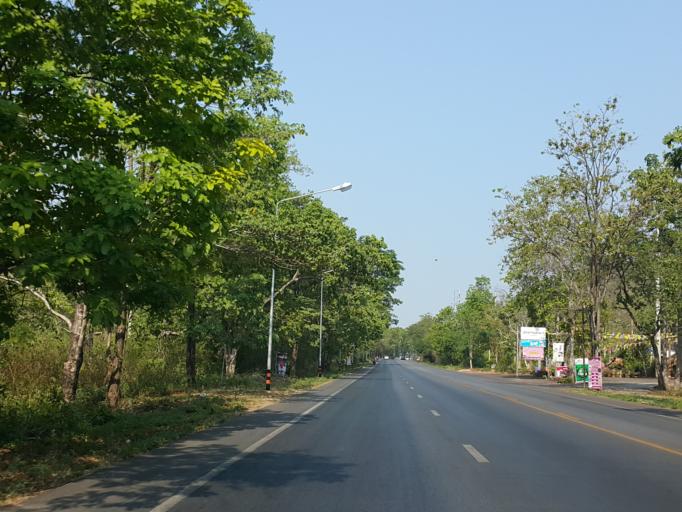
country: TH
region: Kanchanaburi
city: Sai Yok
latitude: 14.1137
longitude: 99.1993
